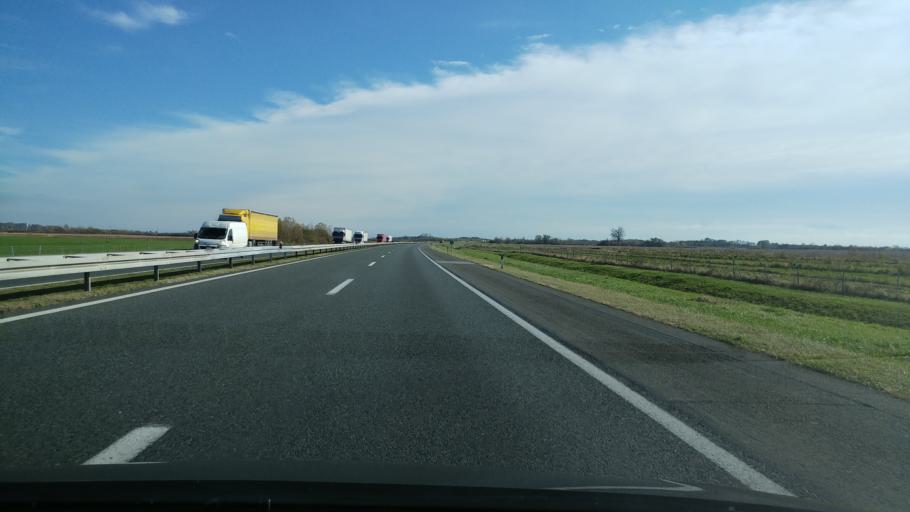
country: HR
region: Brodsko-Posavska
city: Okucani
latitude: 45.2620
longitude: 17.1609
